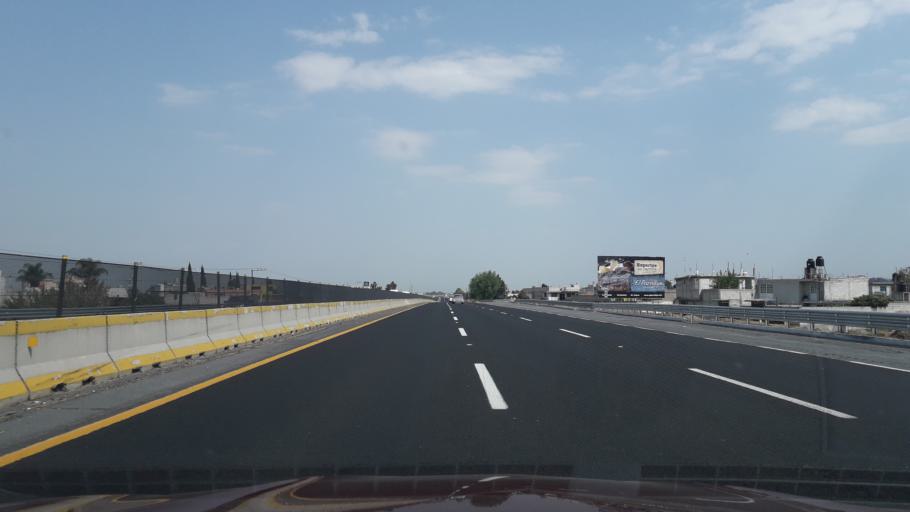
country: MX
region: Puebla
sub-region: San Martin Texmelucan
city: San Rafael Tlanalapan
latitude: 19.2842
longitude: -98.4549
